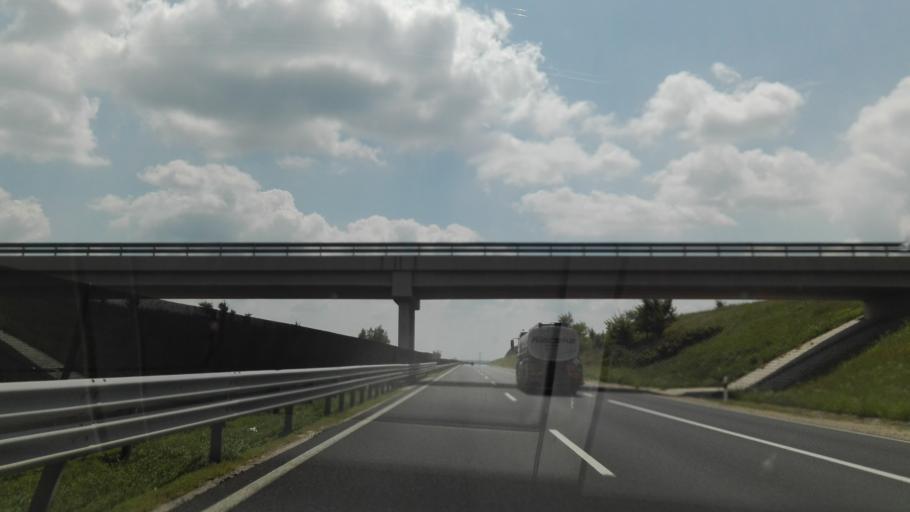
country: HU
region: Fejer
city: Rackeresztur
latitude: 47.2833
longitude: 18.8624
